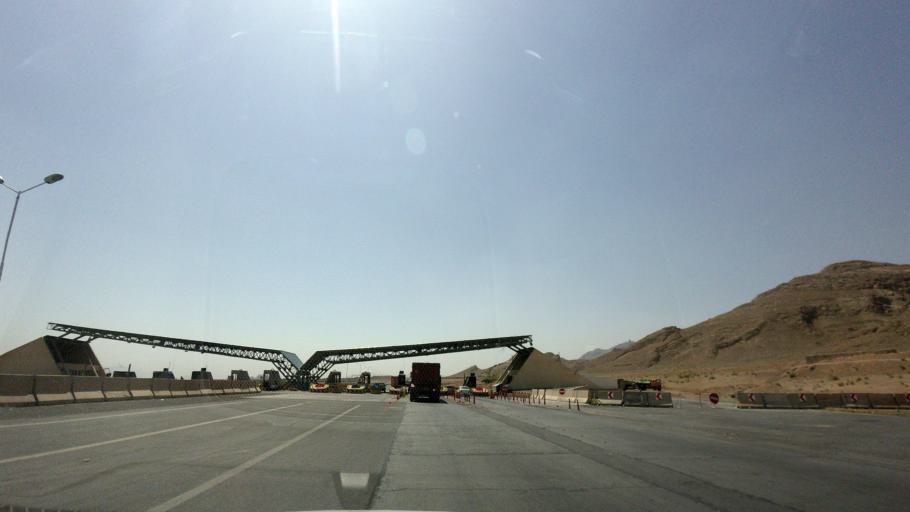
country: IR
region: Isfahan
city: Najafabad
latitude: 32.5828
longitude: 51.2876
